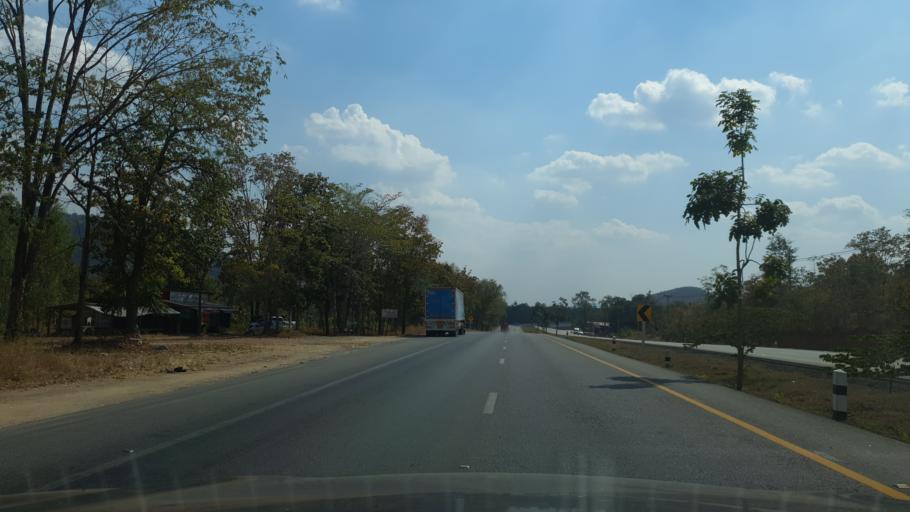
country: TH
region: Lampang
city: Mae Phrik
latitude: 17.3400
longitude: 99.1507
